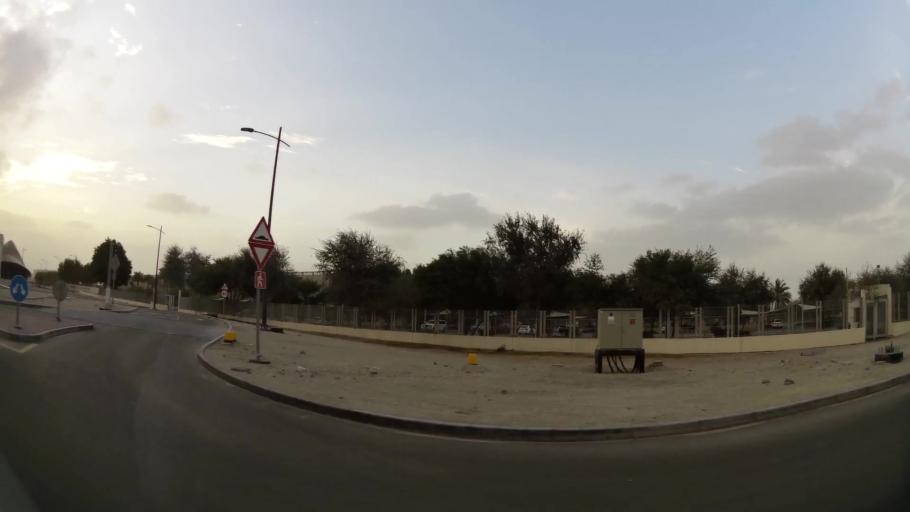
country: AE
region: Abu Dhabi
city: Abu Dhabi
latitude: 24.5335
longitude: 54.4205
